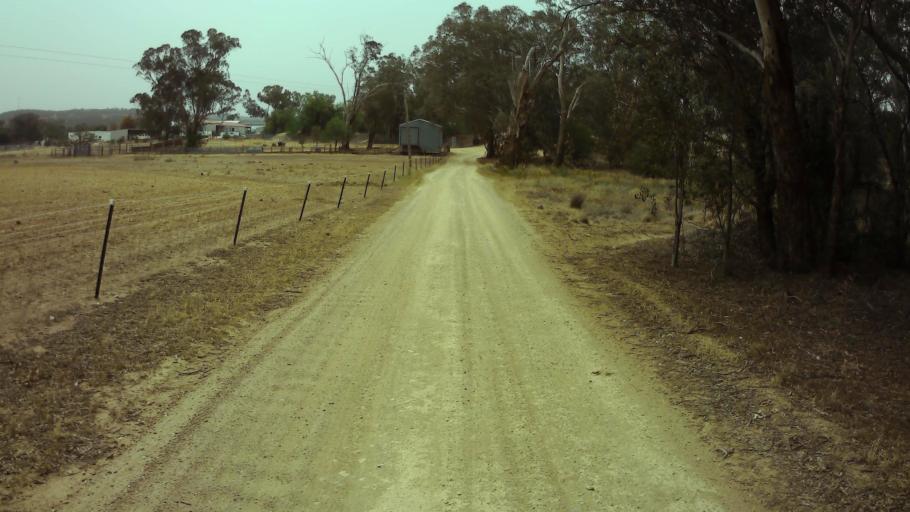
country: AU
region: New South Wales
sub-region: Weddin
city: Grenfell
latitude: -33.9048
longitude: 148.1542
